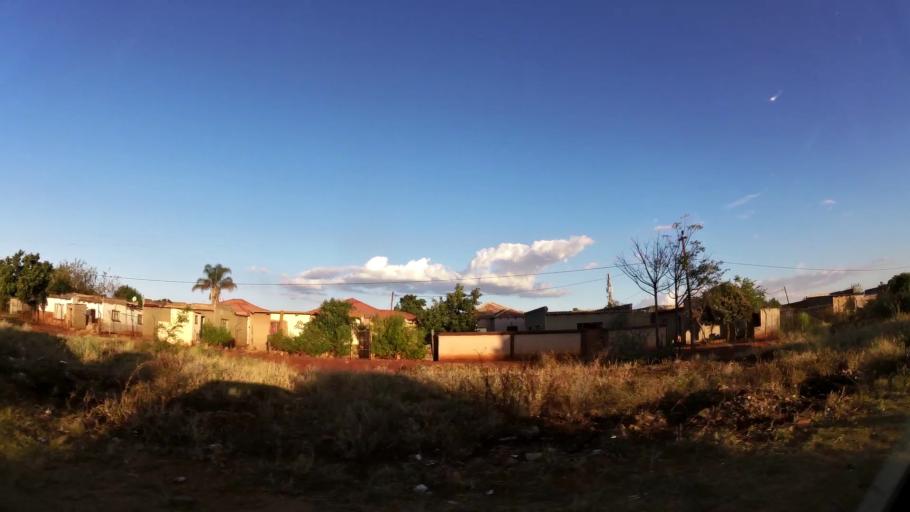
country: ZA
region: Limpopo
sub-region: Waterberg District Municipality
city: Mokopane
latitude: -24.1399
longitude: 28.9968
